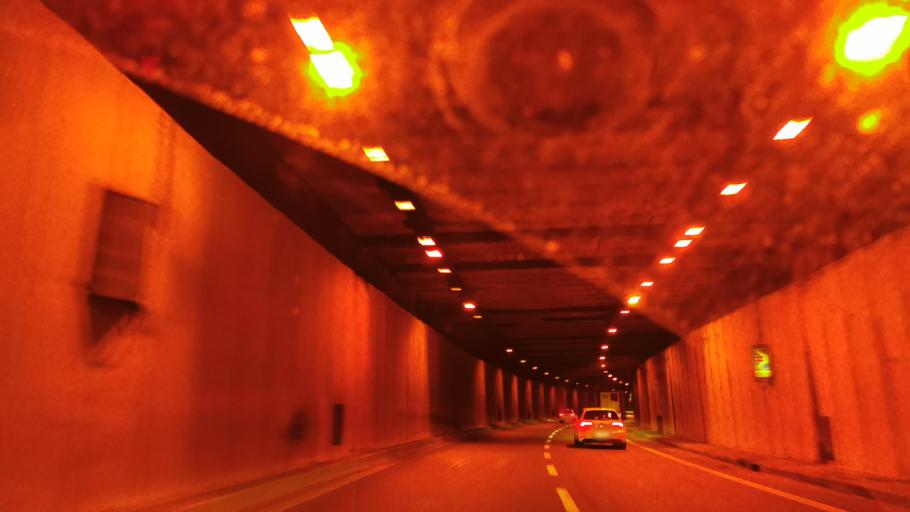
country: IT
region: Lombardy
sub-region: Provincia di Bergamo
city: Ghiaie
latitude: 45.6756
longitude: 9.5751
